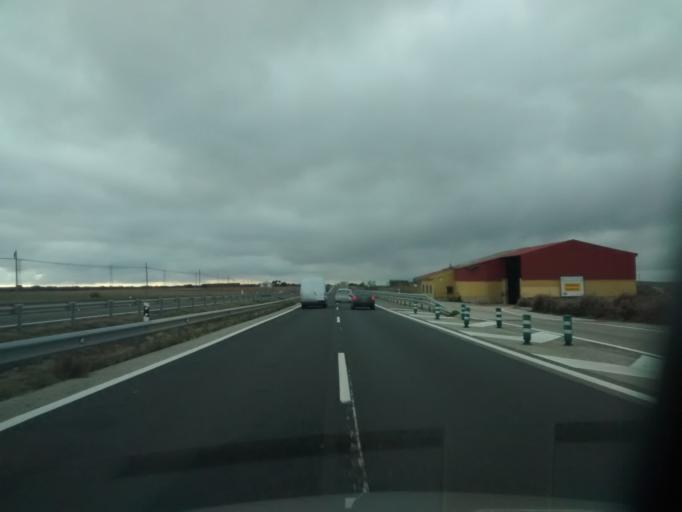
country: ES
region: Castille-La Mancha
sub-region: Provincia de Guadalajara
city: Argecilla
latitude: 40.8751
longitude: -2.8027
